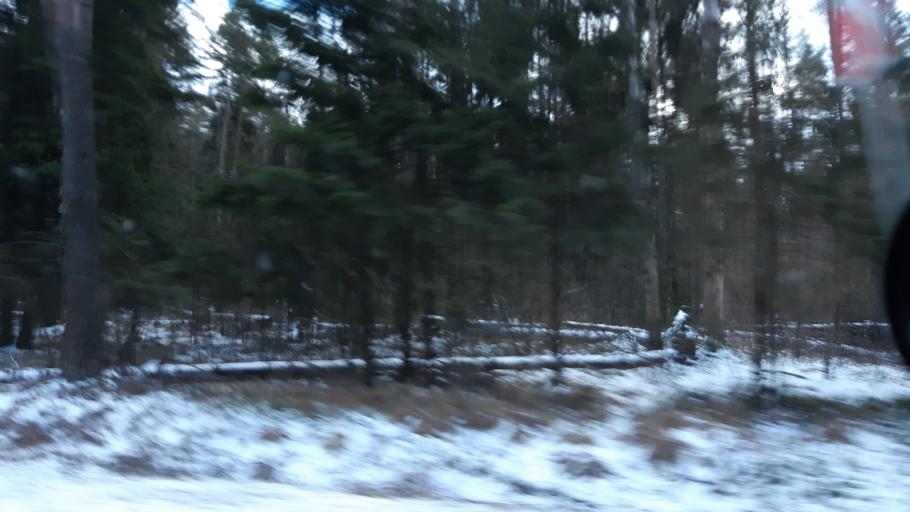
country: RU
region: Moskovskaya
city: Noginsk-9
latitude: 55.9790
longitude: 38.5433
